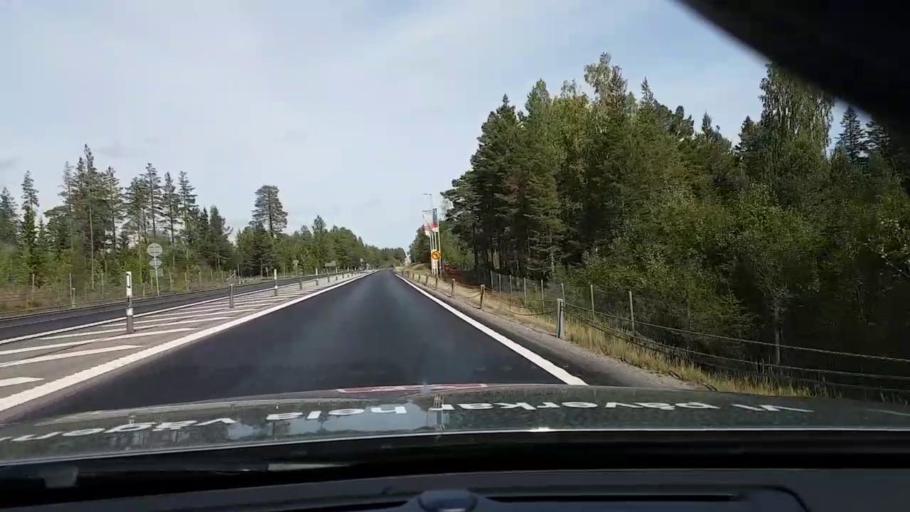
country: SE
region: Vaesternorrland
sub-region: OErnskoeldsviks Kommun
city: Husum
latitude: 63.4797
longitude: 19.2949
